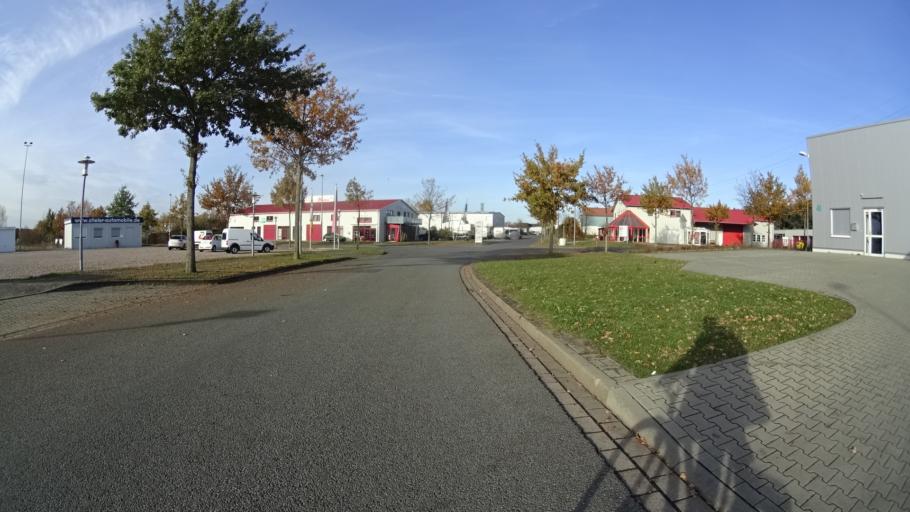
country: DE
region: Lower Saxony
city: Wendisch Evern
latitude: 53.2371
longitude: 10.4646
